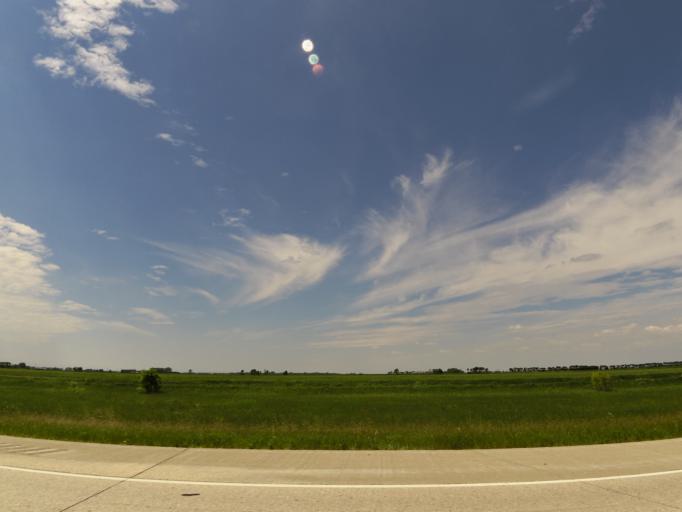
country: US
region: North Dakota
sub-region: Walsh County
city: Grafton
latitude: 48.3667
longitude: -97.1896
